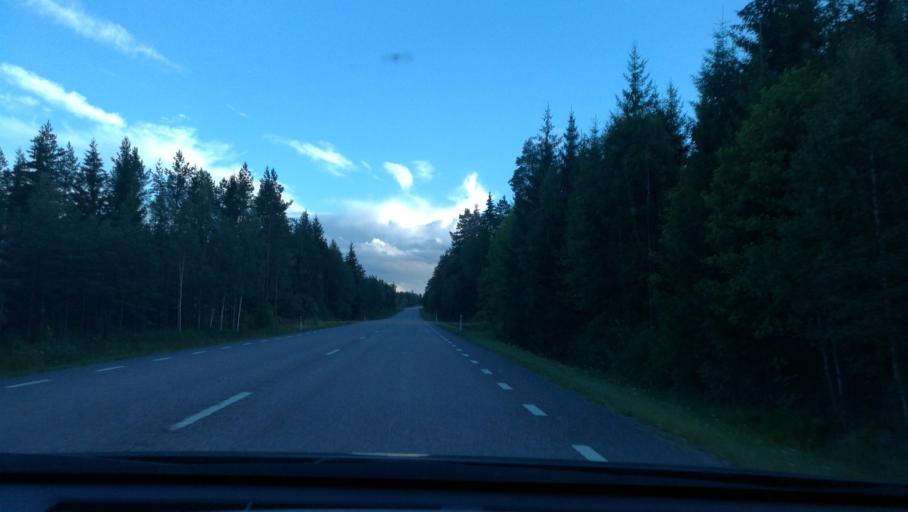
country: SE
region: Soedermanland
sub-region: Katrineholms Kommun
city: Katrineholm
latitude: 59.0505
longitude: 16.2212
